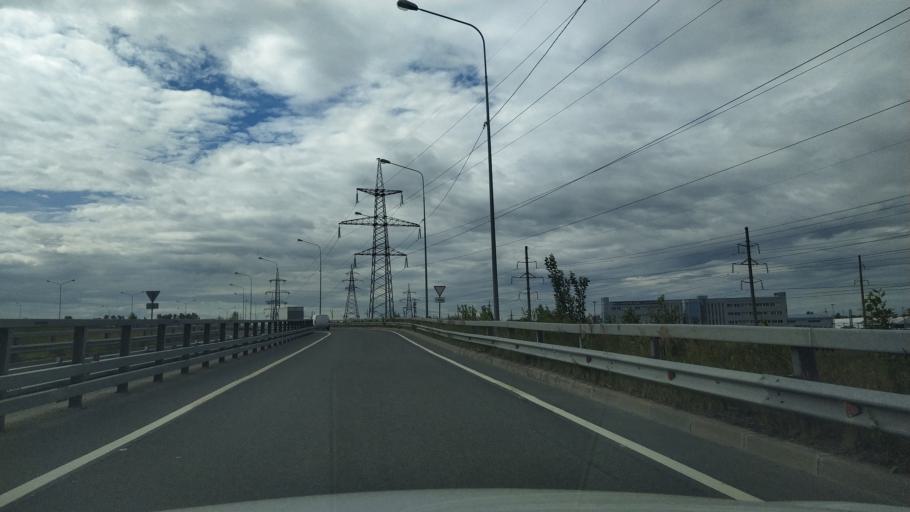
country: RU
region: Leningrad
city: Murino
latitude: 60.0171
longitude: 30.4583
